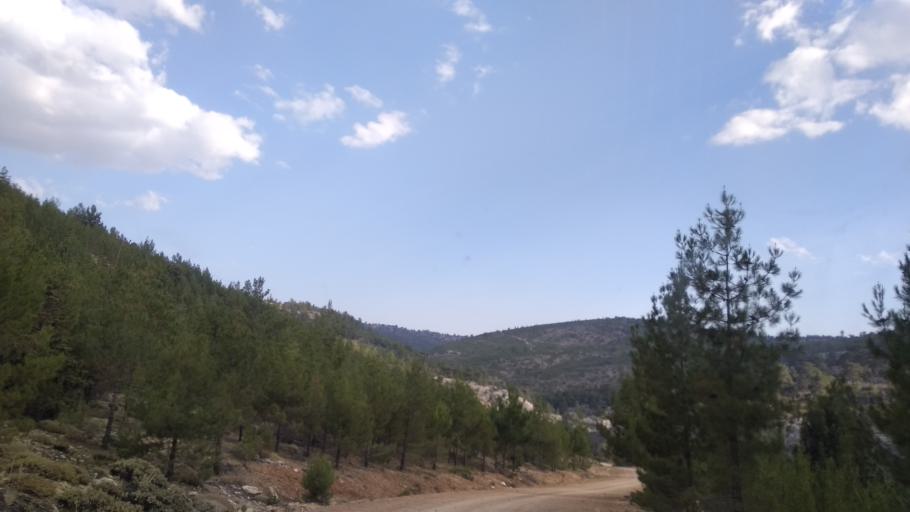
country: TR
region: Mersin
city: Sarikavak
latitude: 36.5982
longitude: 33.7124
